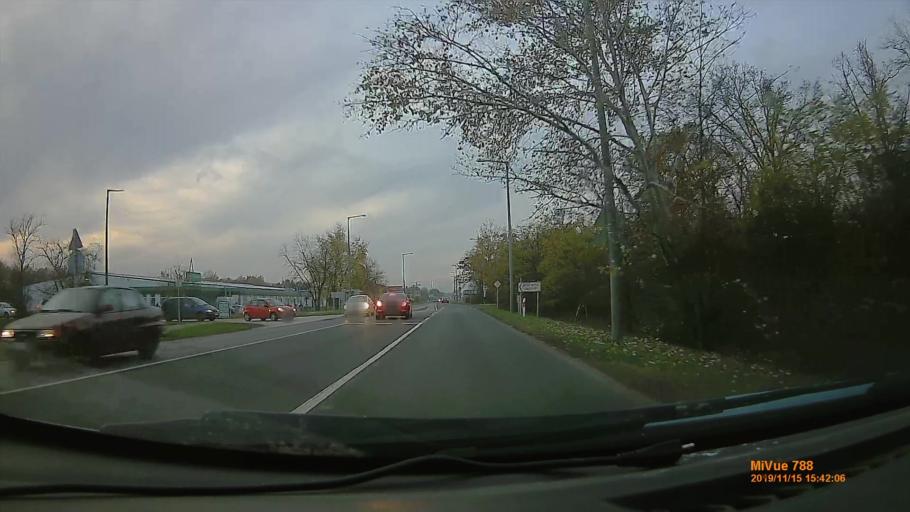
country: HU
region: Bekes
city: Bekescsaba
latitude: 46.6767
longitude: 21.1291
